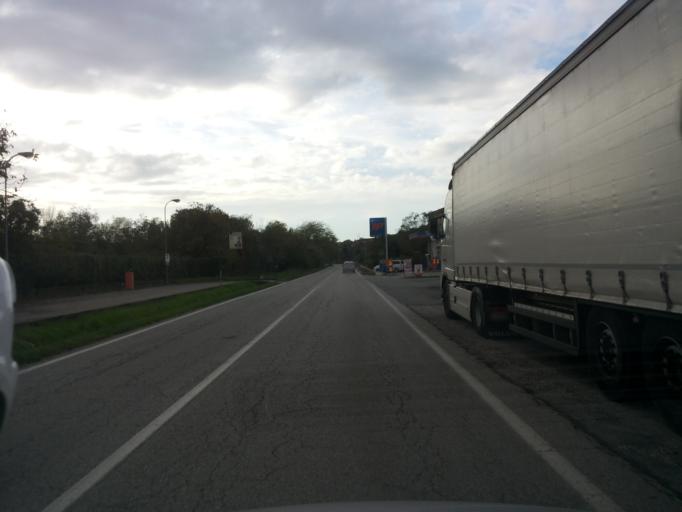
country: IT
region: Piedmont
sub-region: Provincia di Alessandria
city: San Giorgio Monferrato
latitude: 45.1015
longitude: 8.4195
